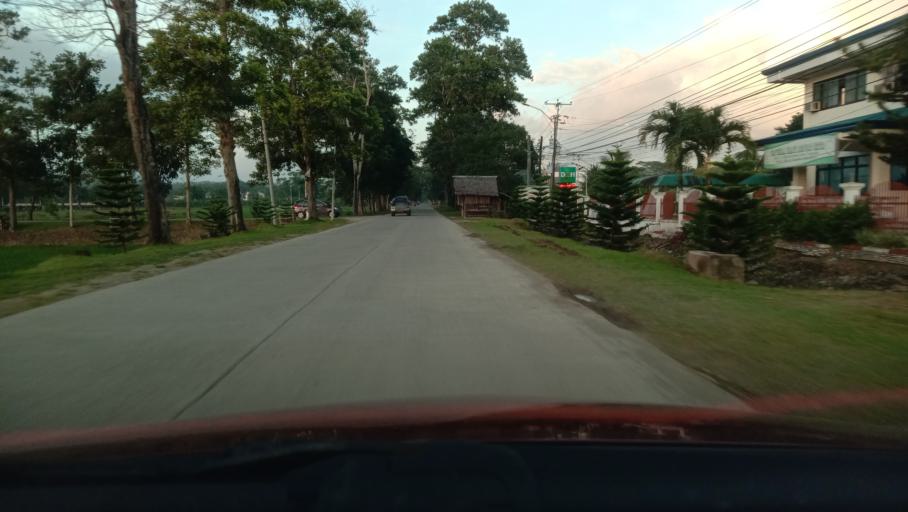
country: PH
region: Caraga
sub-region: Province of Agusan del Sur
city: Patin-ay
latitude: 8.5475
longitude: 125.9421
